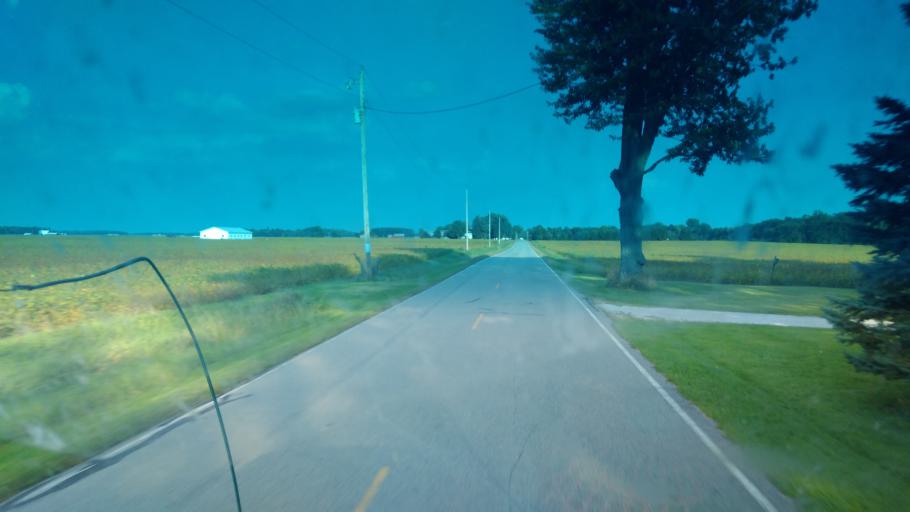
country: US
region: Ohio
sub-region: Crawford County
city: Bucyrus
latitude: 40.9649
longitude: -83.0312
